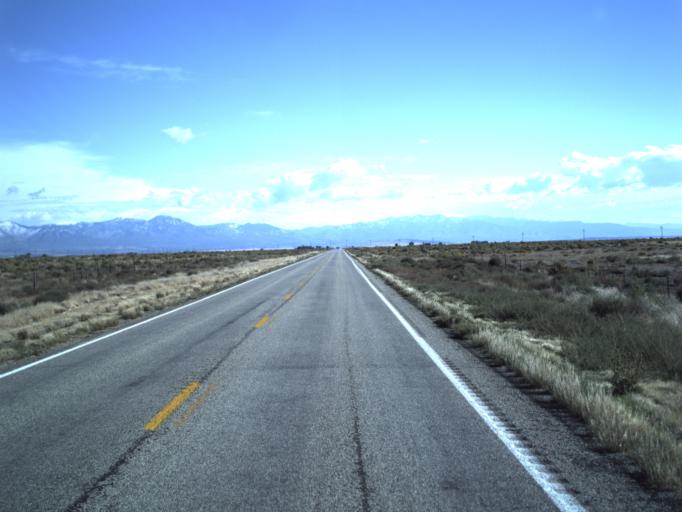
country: US
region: Utah
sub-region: Millard County
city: Delta
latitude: 39.2391
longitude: -112.4323
